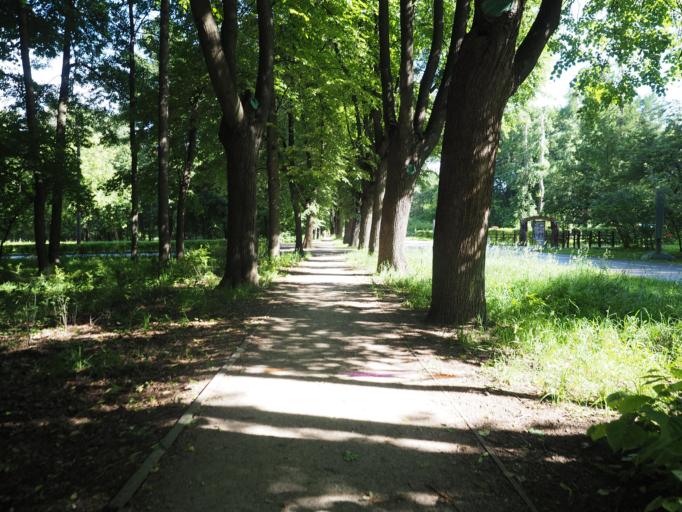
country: RU
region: Moskovskaya
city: Bogorodskoye
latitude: 55.7826
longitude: 37.7478
